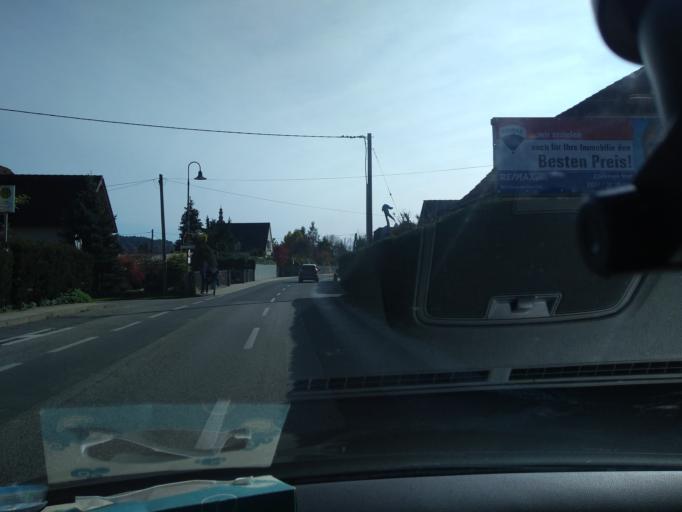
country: AT
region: Styria
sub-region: Politischer Bezirk Graz-Umgebung
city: Fernitz
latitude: 46.9770
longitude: 15.4969
